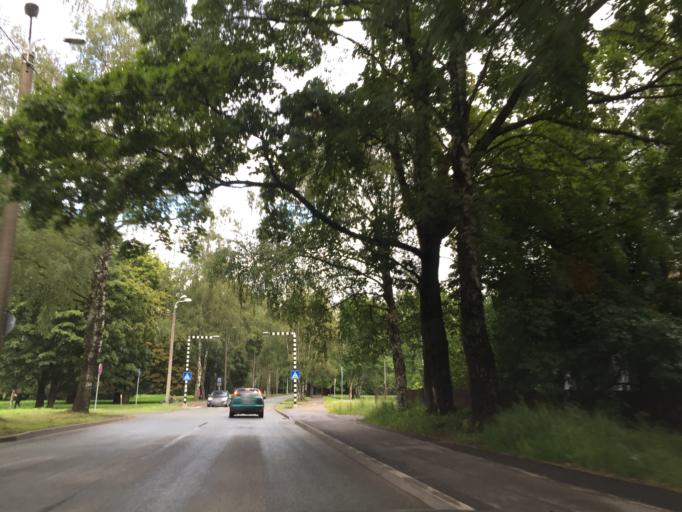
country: LV
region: Marupe
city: Marupe
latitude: 56.9535
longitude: 24.0084
